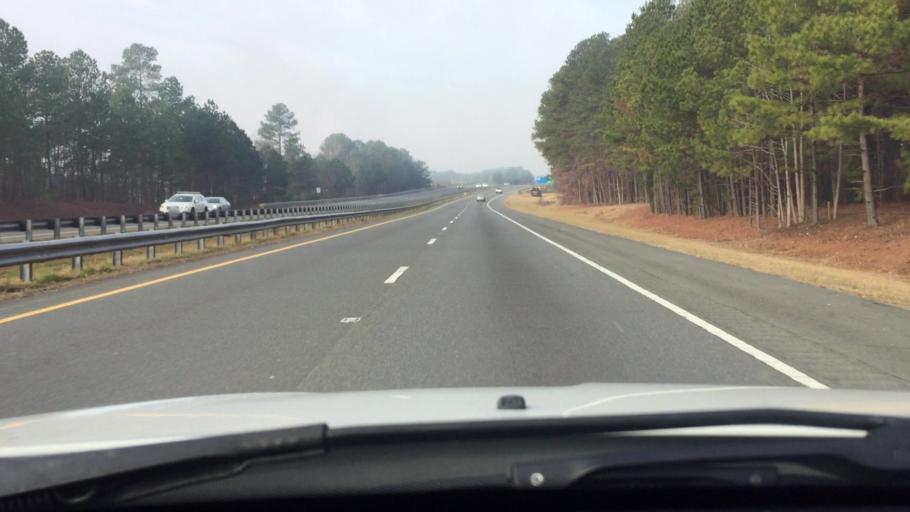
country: US
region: North Carolina
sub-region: Wake County
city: Holly Springs
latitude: 35.6439
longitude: -78.9957
